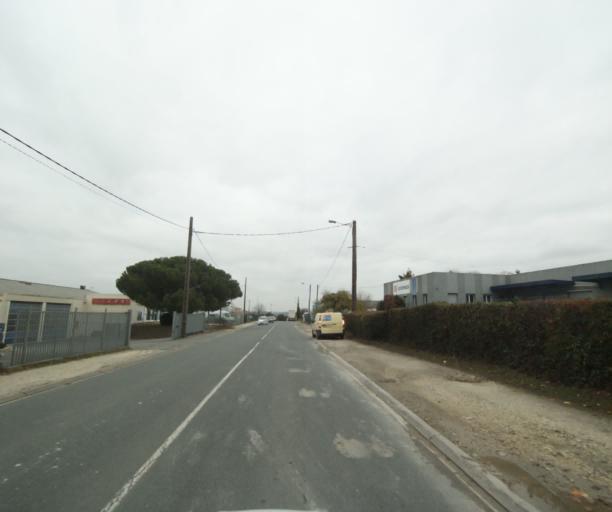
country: FR
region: Poitou-Charentes
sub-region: Departement de la Charente-Maritime
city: Les Gonds
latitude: 45.7212
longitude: -0.6428
